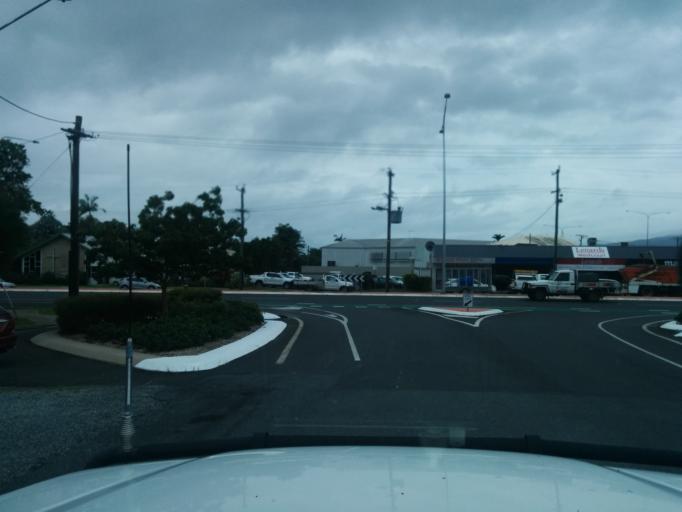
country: AU
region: Queensland
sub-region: Cairns
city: Cairns
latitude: -16.9297
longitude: 145.7573
